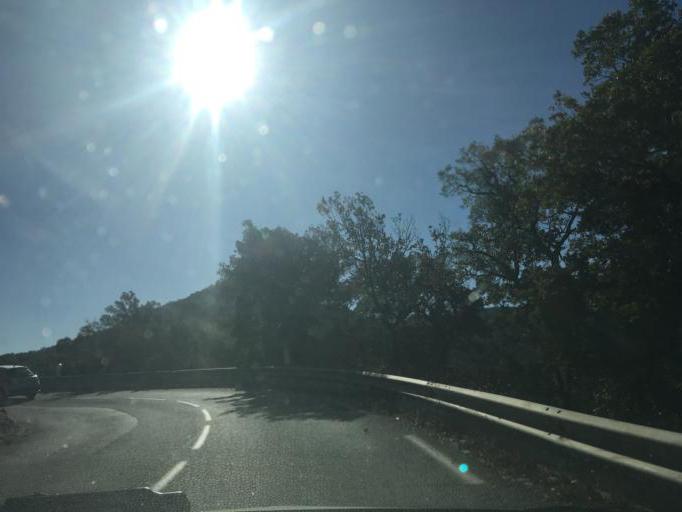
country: FR
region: Provence-Alpes-Cote d'Azur
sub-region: Departement du Var
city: La Garde-Freinet
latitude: 43.3307
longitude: 6.4578
